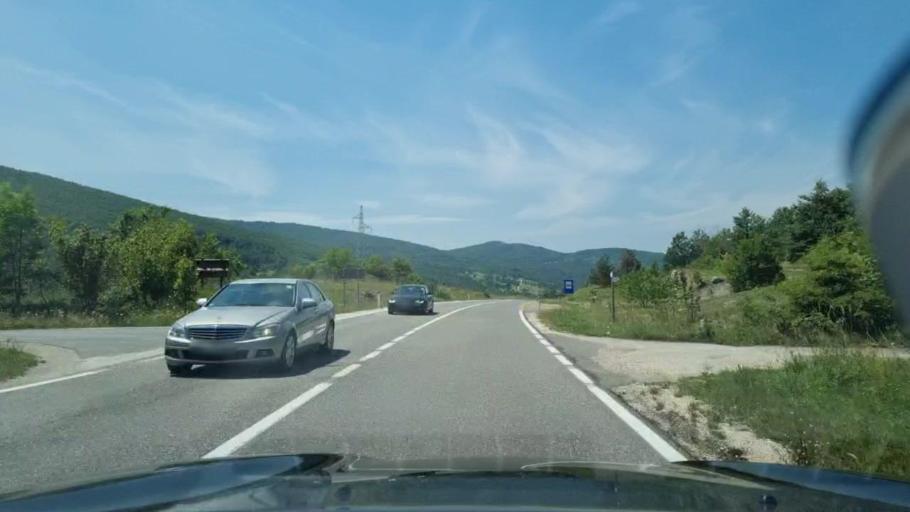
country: BA
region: Federation of Bosnia and Herzegovina
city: Sanica
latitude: 44.5541
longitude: 16.5225
